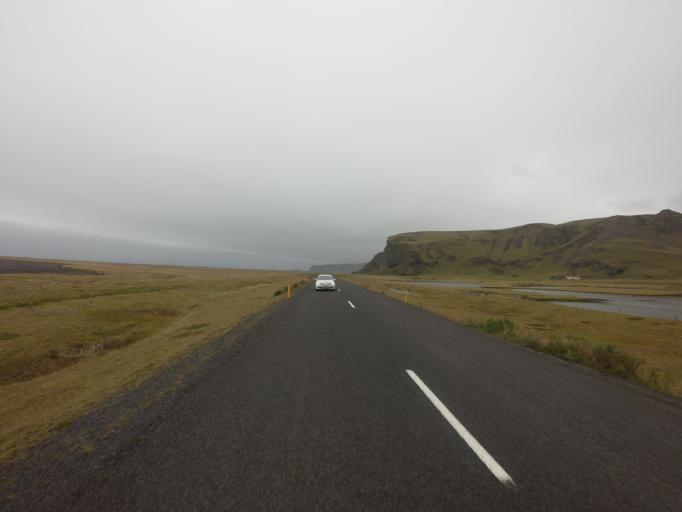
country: IS
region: South
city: Vestmannaeyjar
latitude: 63.4230
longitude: -18.9110
